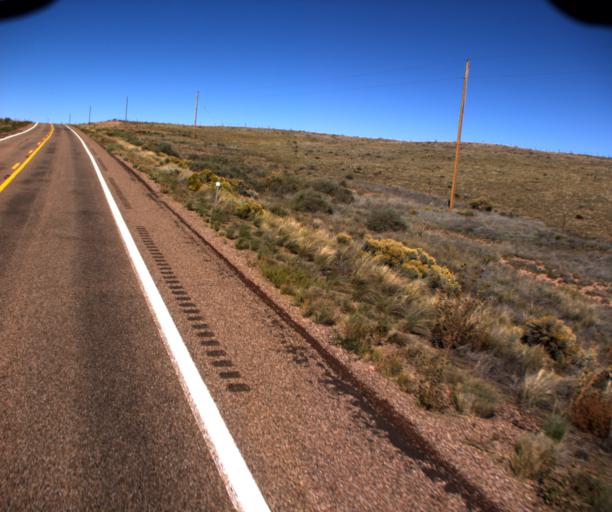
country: US
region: Arizona
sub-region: Apache County
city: Saint Johns
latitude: 34.5302
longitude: -109.4592
